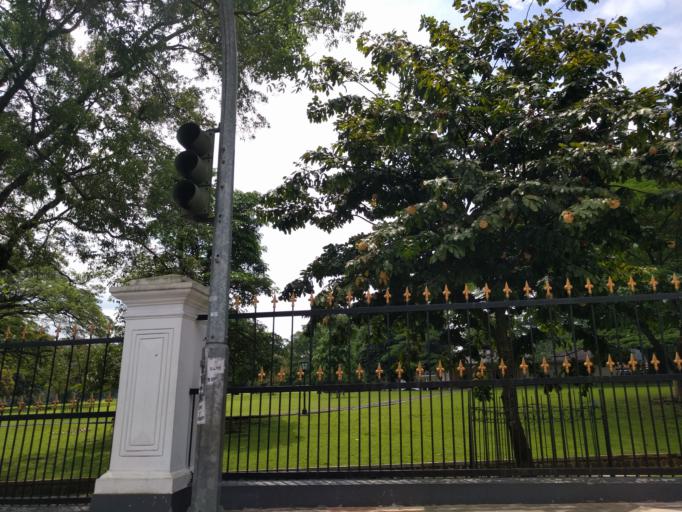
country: ID
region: West Java
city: Bogor
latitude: -6.5968
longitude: 106.7939
